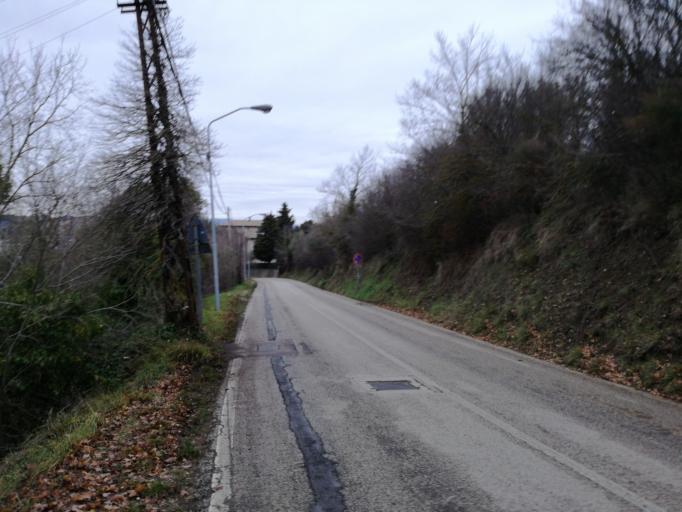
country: IT
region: Umbria
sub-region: Provincia di Perugia
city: Perugia
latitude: 43.1230
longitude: 12.3791
